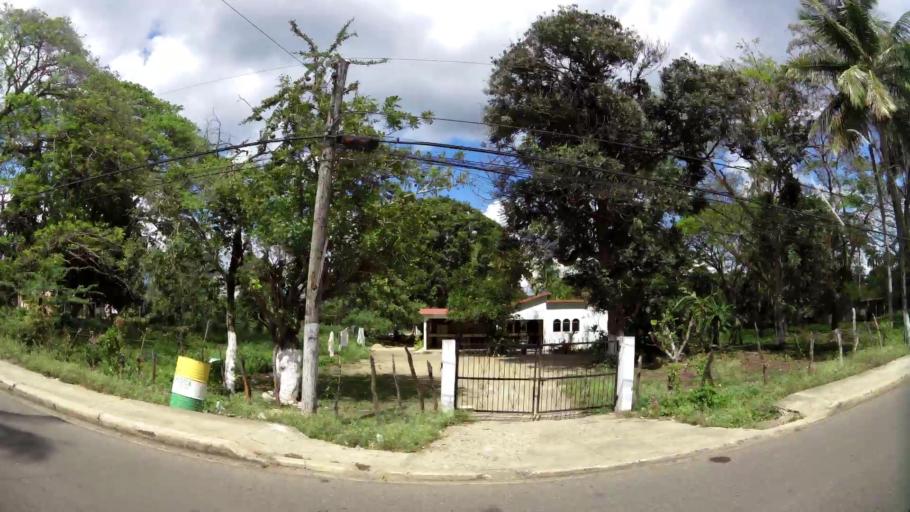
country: DO
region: Santiago
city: Santiago de los Caballeros
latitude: 19.4045
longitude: -70.6611
